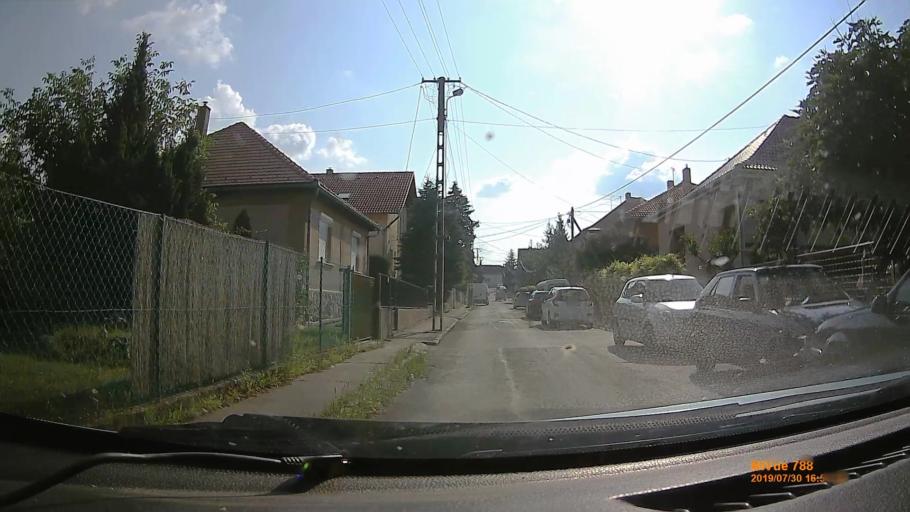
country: HU
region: Baranya
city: Pecs
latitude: 46.0736
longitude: 18.2029
